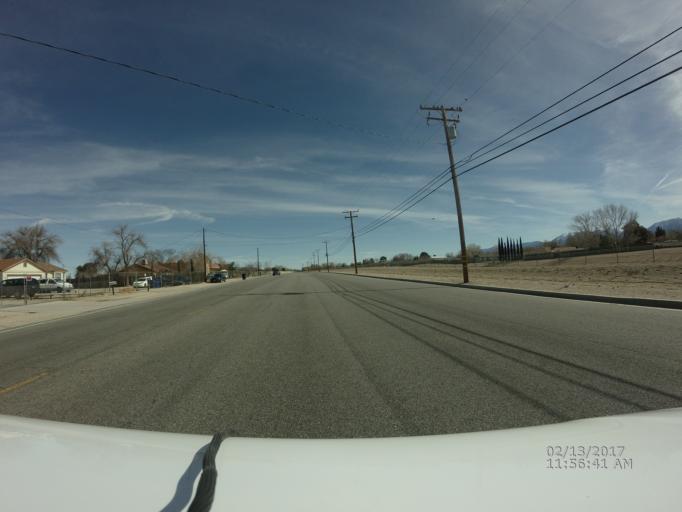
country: US
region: California
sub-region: Los Angeles County
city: Littlerock
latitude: 34.5579
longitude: -117.9626
